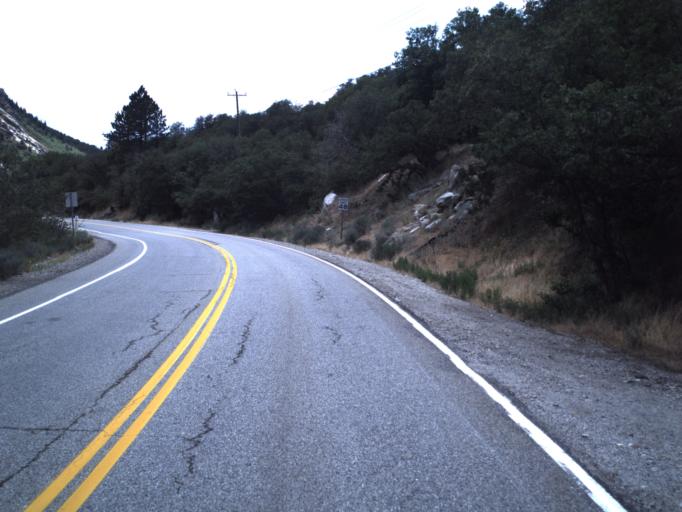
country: US
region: Utah
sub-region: Salt Lake County
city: Granite
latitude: 40.5720
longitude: -111.7687
